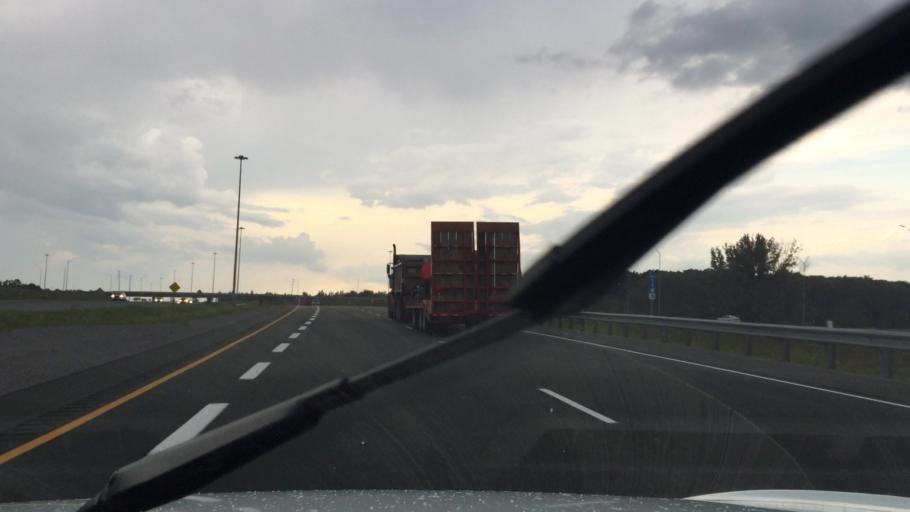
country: CA
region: Ontario
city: Ajax
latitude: 43.9510
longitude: -79.0129
